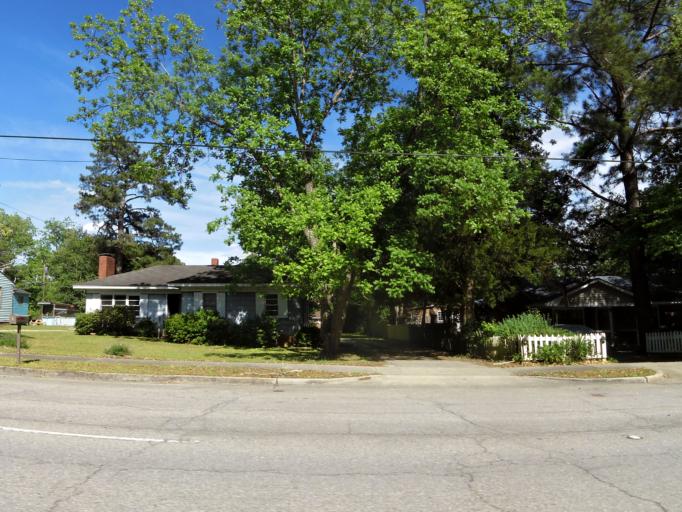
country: US
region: South Carolina
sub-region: Bamberg County
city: Denmark
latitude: 33.3058
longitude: -81.1448
